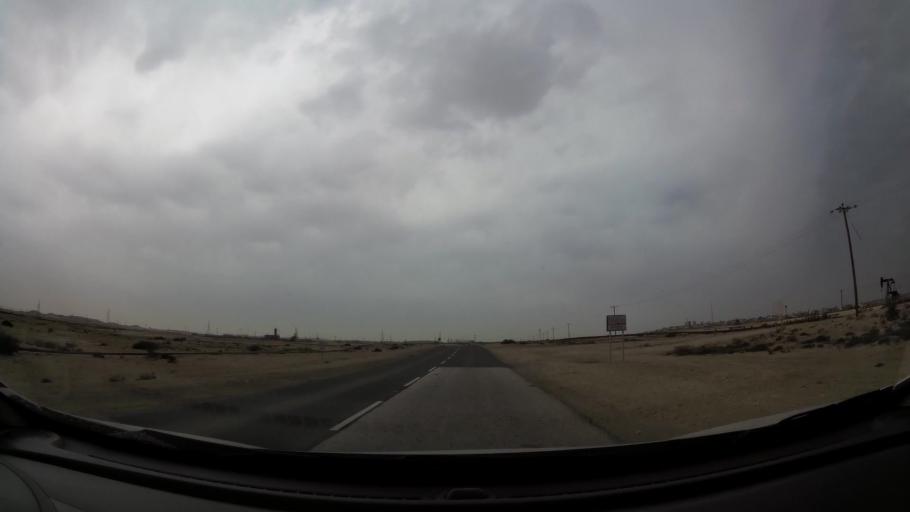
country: BH
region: Northern
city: Ar Rifa'
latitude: 26.0844
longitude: 50.5662
